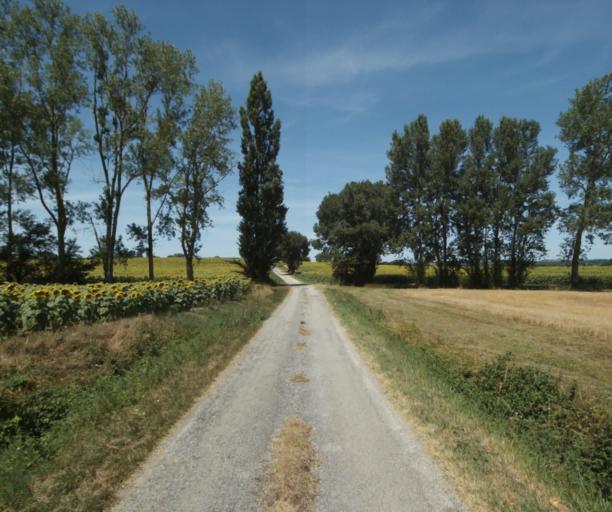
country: FR
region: Midi-Pyrenees
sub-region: Departement de la Haute-Garonne
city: Revel
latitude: 43.4941
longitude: 2.0347
